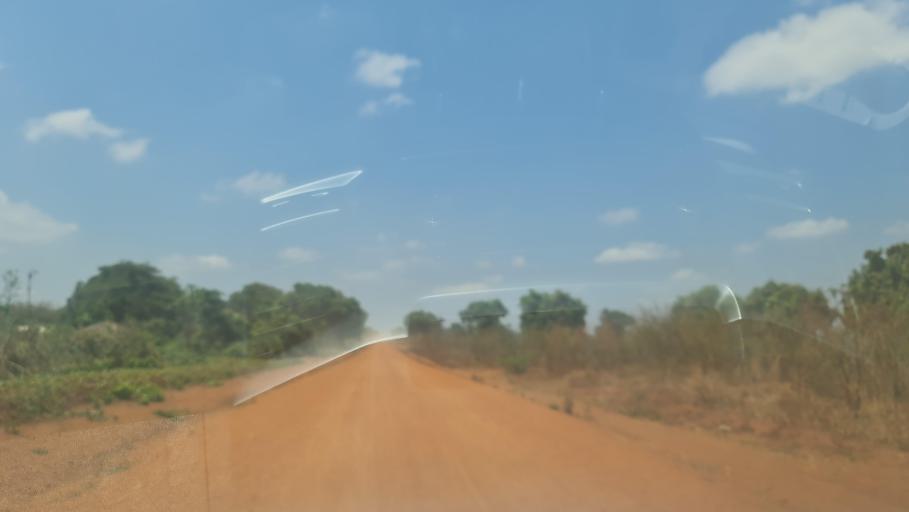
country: MW
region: Southern Region
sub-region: Nsanje District
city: Nsanje
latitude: -17.3335
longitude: 35.7170
